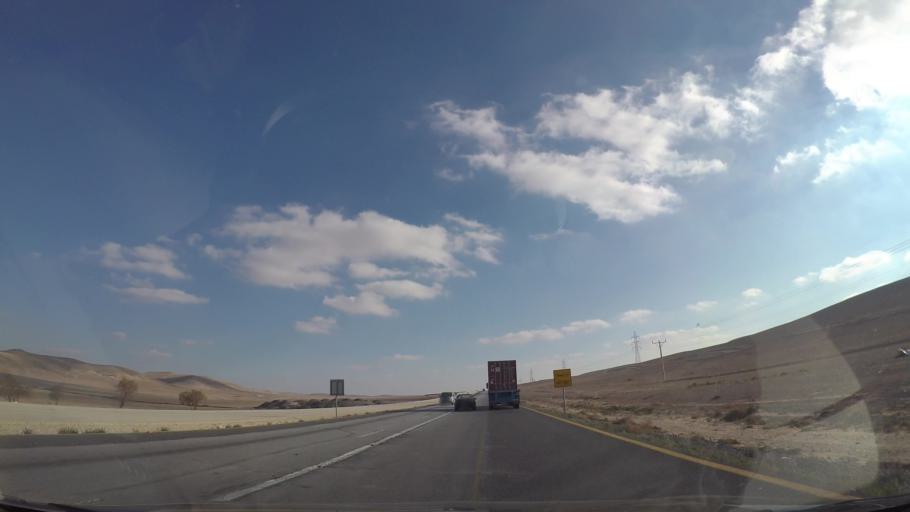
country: JO
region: Karak
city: Karak City
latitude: 31.1821
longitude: 36.0190
